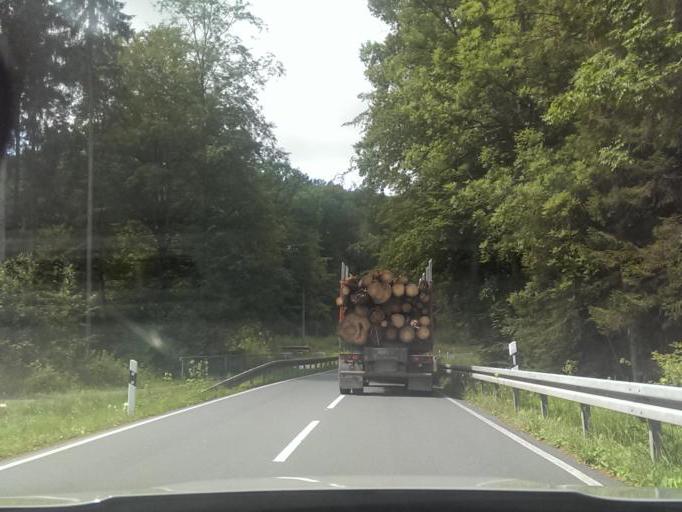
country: DE
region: North Rhine-Westphalia
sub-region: Regierungsbezirk Detmold
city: Hoexter
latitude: 51.8271
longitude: 9.3609
